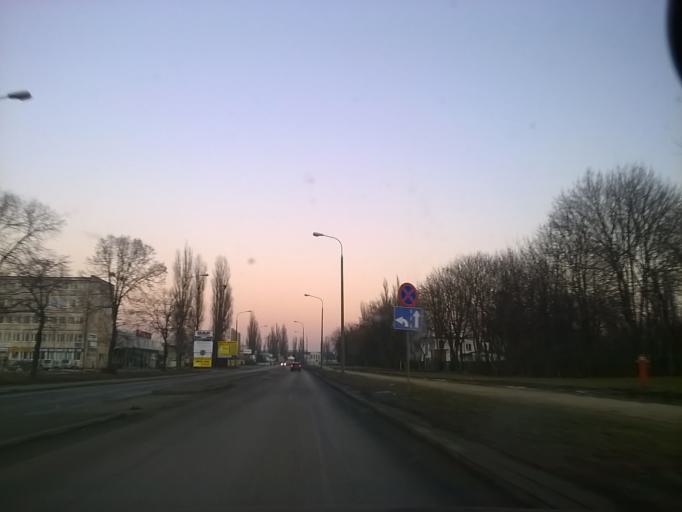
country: PL
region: Warmian-Masurian Voivodeship
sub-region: Powiat olsztynski
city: Olsztyn
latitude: 53.7860
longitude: 20.5323
